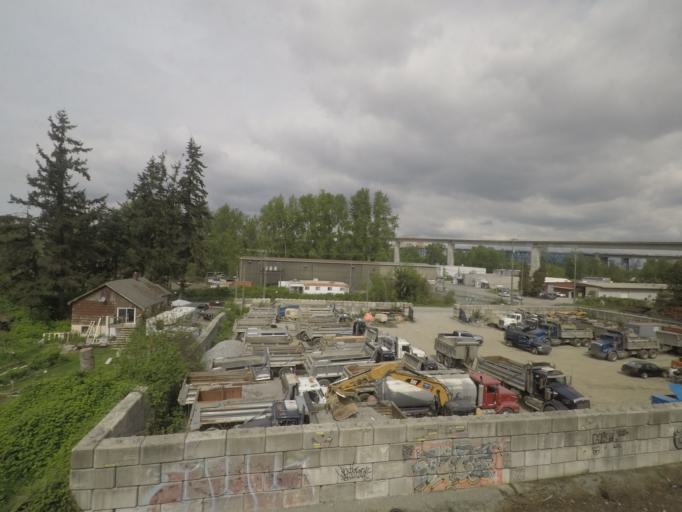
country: CA
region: British Columbia
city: New Westminster
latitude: 49.2014
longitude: -122.8889
